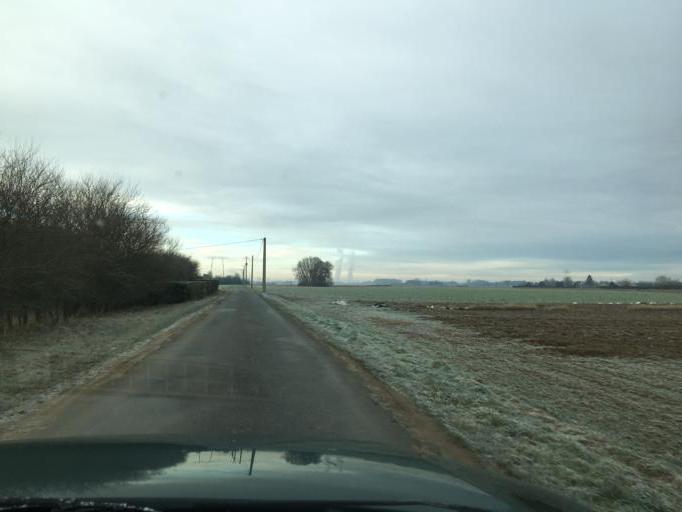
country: FR
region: Centre
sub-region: Departement du Loiret
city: Lailly-en-Val
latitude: 47.7898
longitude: 1.6878
